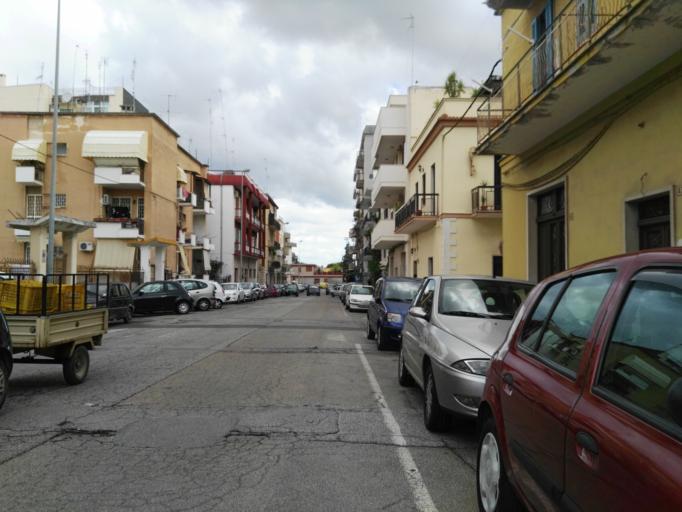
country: IT
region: Apulia
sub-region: Provincia di Bari
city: Triggiano
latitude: 41.0615
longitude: 16.9169
